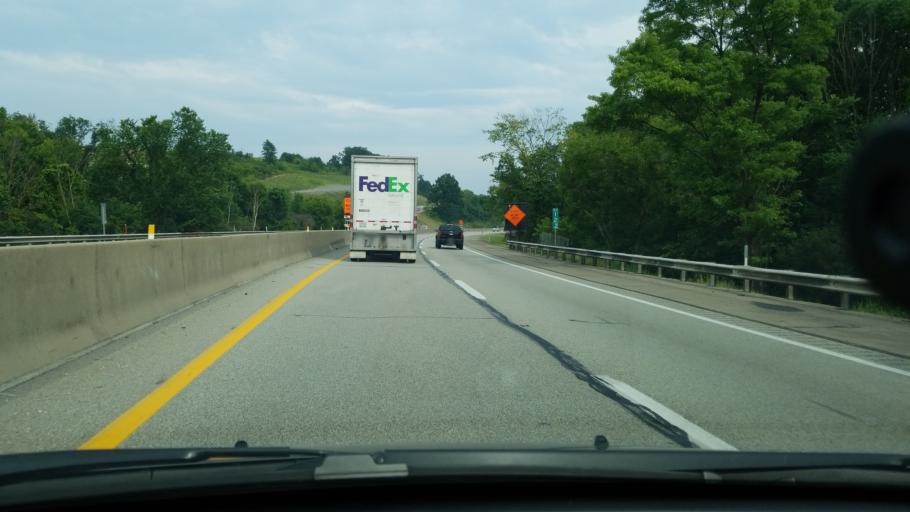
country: US
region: Pennsylvania
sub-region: Beaver County
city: Big Beaver
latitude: 40.8190
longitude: -80.3357
